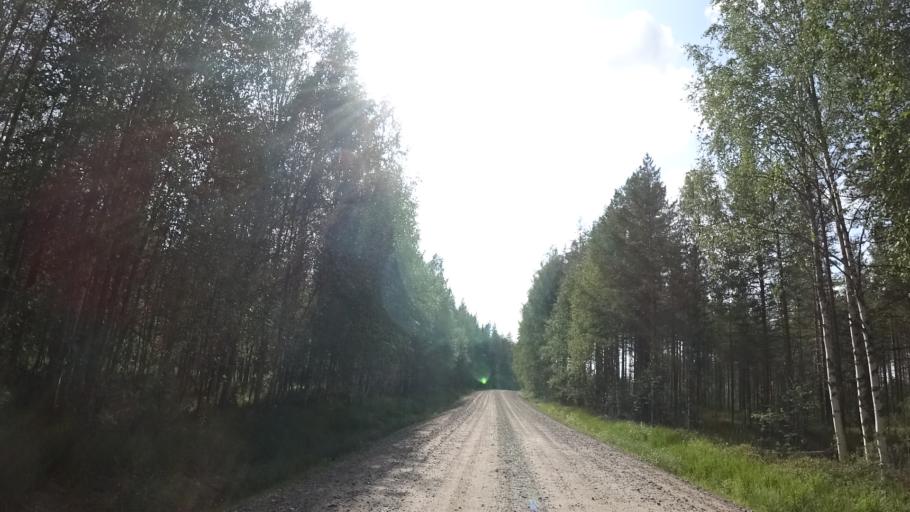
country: FI
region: North Karelia
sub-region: Pielisen Karjala
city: Lieksa
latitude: 63.5683
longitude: 30.0961
